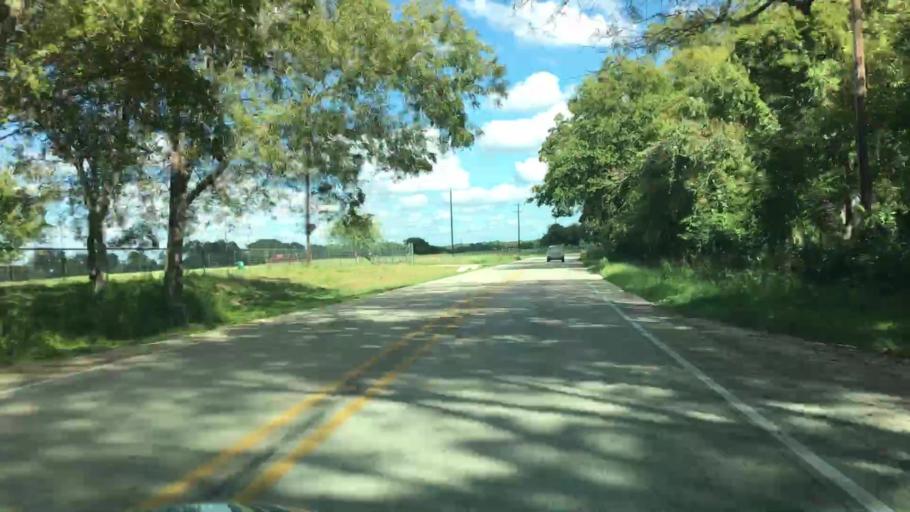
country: US
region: Texas
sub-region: Blanco County
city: Blanco
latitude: 30.0921
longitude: -98.3935
